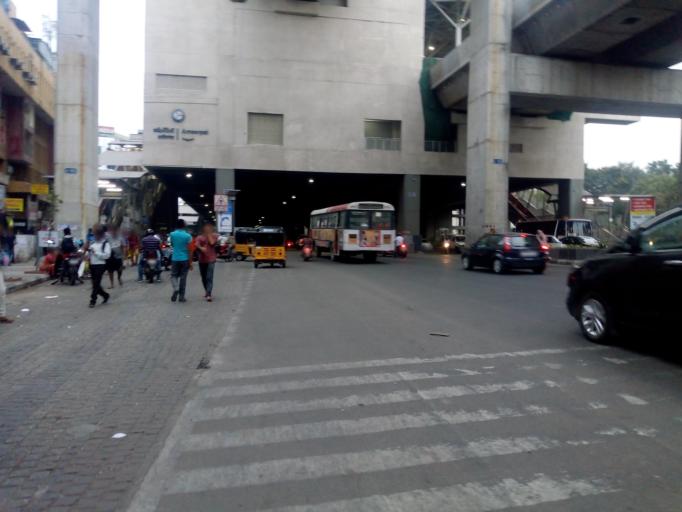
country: IN
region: Telangana
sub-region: Hyderabad
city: Hyderabad
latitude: 17.4366
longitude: 78.4442
